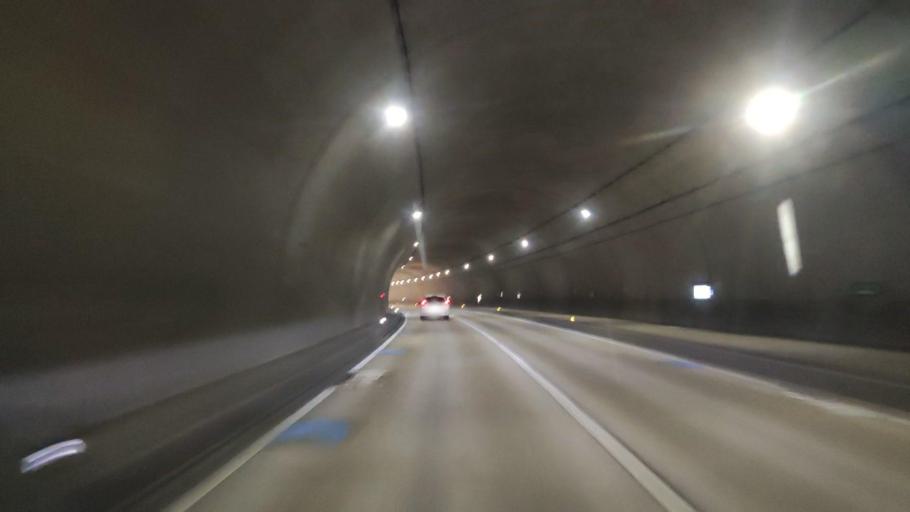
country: JP
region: Wakayama
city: Shingu
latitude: 33.7387
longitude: 135.9902
